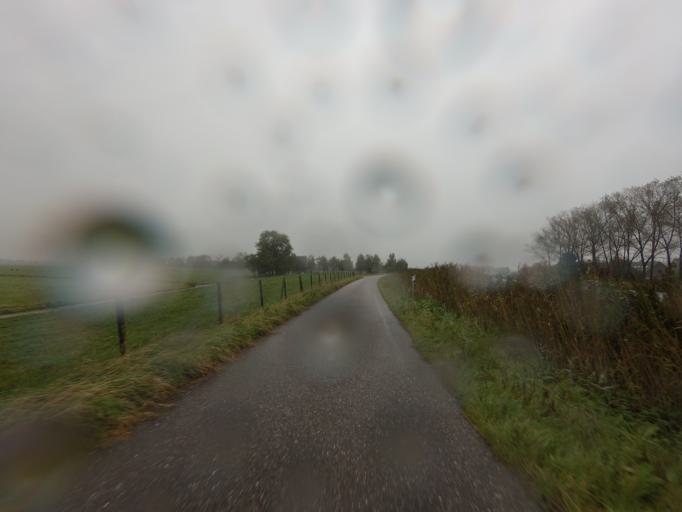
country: NL
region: South Holland
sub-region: Gemeente Leerdam
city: Leerdam
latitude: 51.9359
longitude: 5.0361
